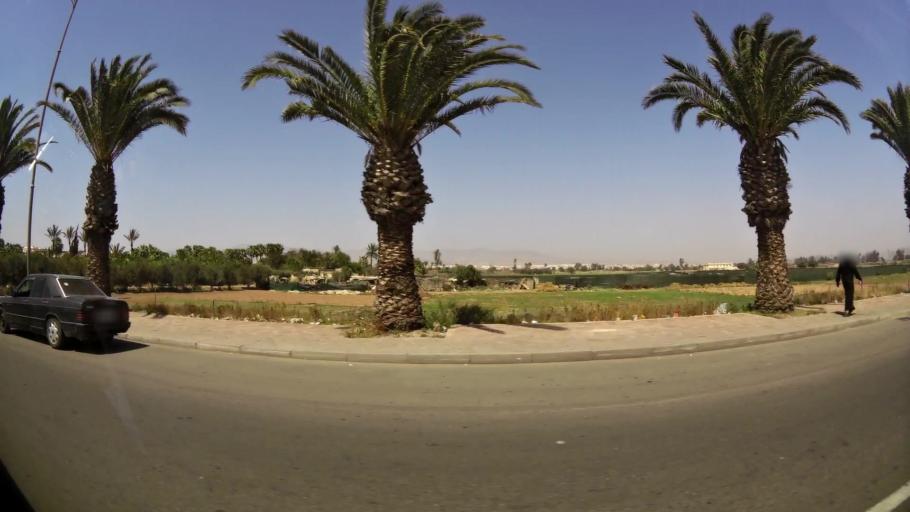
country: MA
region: Souss-Massa-Draa
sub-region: Inezgane-Ait Mellou
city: Inezgane
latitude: 30.3592
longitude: -9.5235
